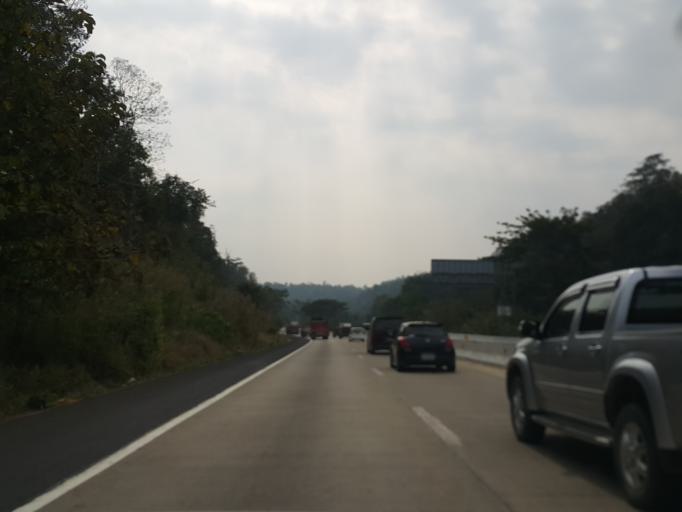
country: TH
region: Lamphun
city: Mae Tha
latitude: 18.3853
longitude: 99.2204
